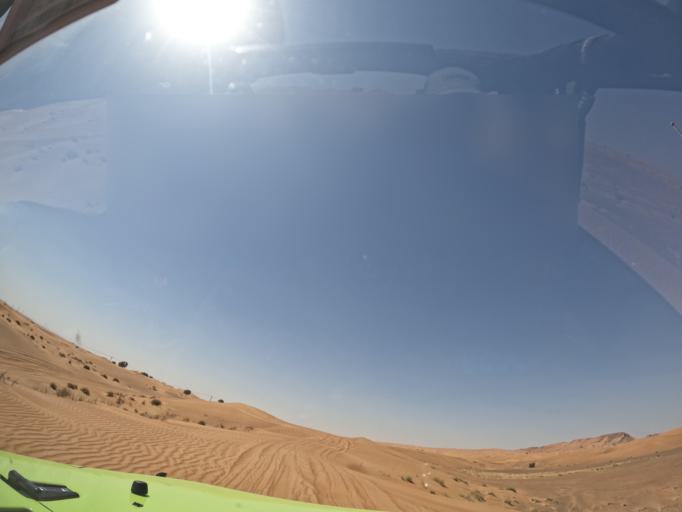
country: AE
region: Ash Shariqah
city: Adh Dhayd
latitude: 25.0192
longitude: 55.7489
